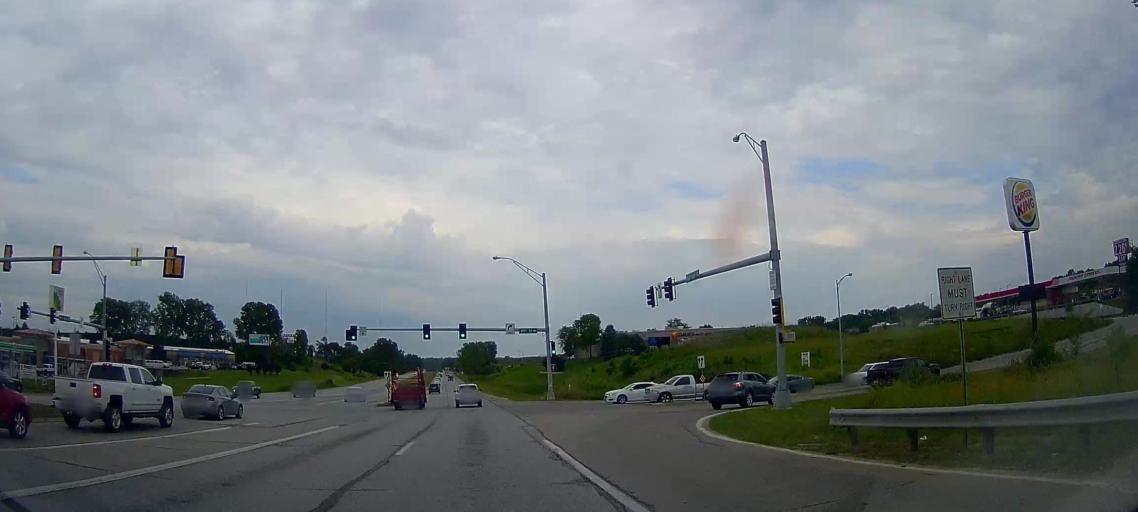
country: US
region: Nebraska
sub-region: Douglas County
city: Bennington
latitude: 41.3191
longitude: -96.0652
